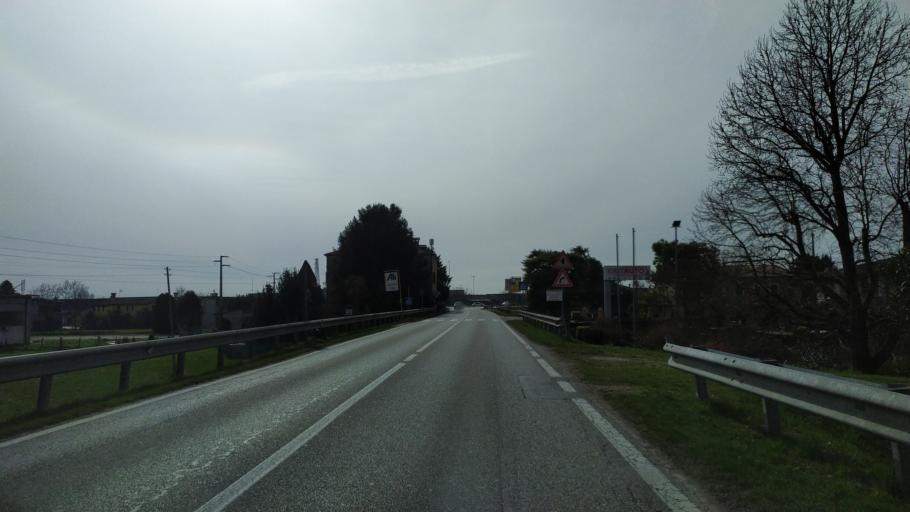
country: IT
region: Veneto
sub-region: Provincia di Padova
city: Tavo
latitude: 45.4886
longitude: 11.8567
